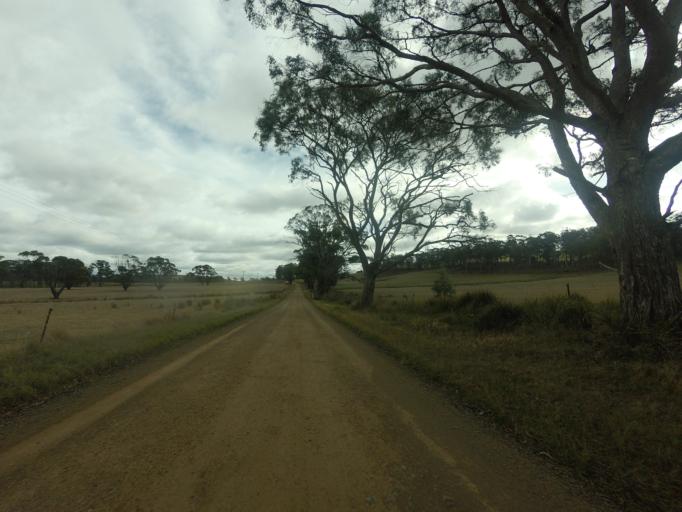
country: AU
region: Tasmania
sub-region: Sorell
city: Sorell
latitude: -42.4296
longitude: 147.4577
